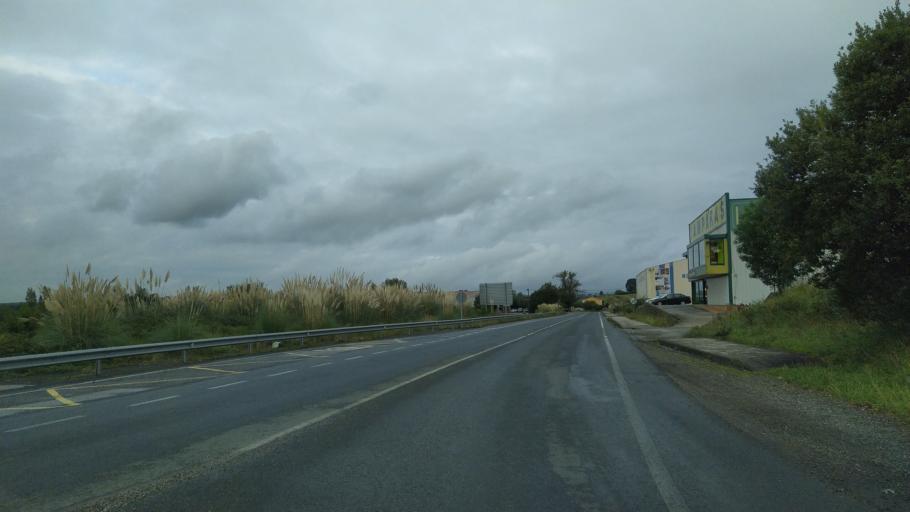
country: ES
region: Cantabria
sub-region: Provincia de Cantabria
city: El Astillero
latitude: 43.3976
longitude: -3.7832
